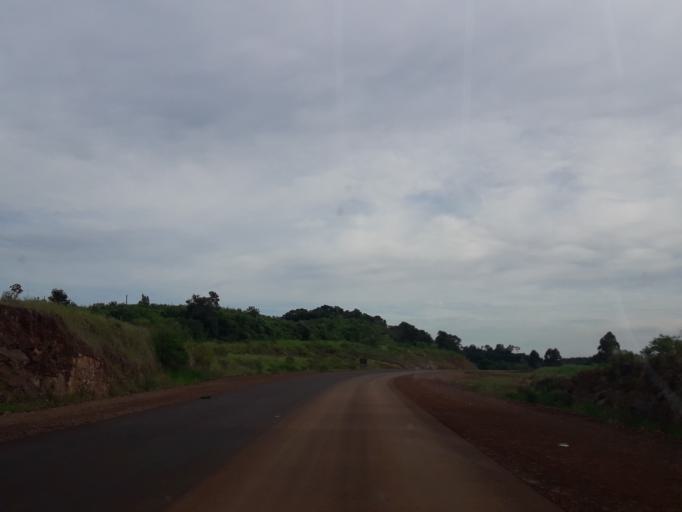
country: AR
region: Misiones
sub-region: Departamento de San Pedro
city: San Pedro
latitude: -26.5347
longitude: -53.9406
